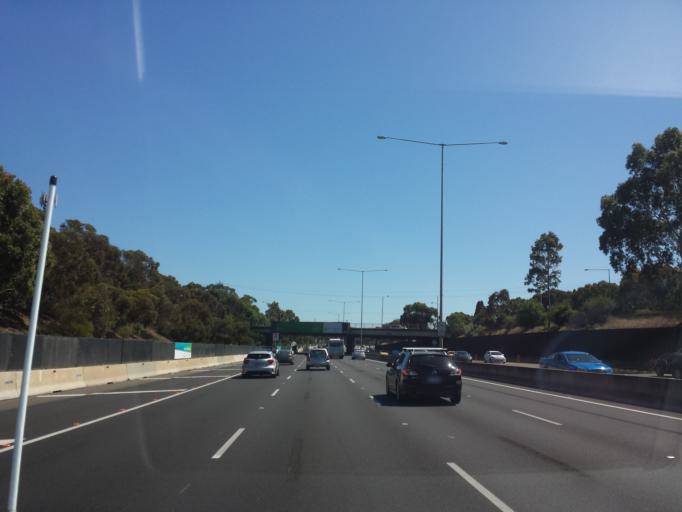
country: AU
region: Victoria
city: Brunswick West
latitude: -37.7534
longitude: 144.9362
